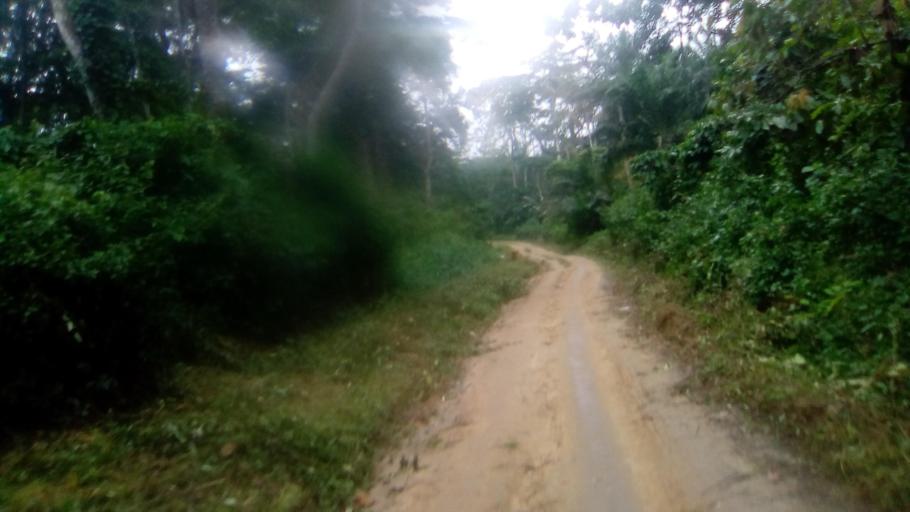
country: SL
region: Eastern Province
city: Kailahun
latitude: 8.2940
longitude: -10.6014
